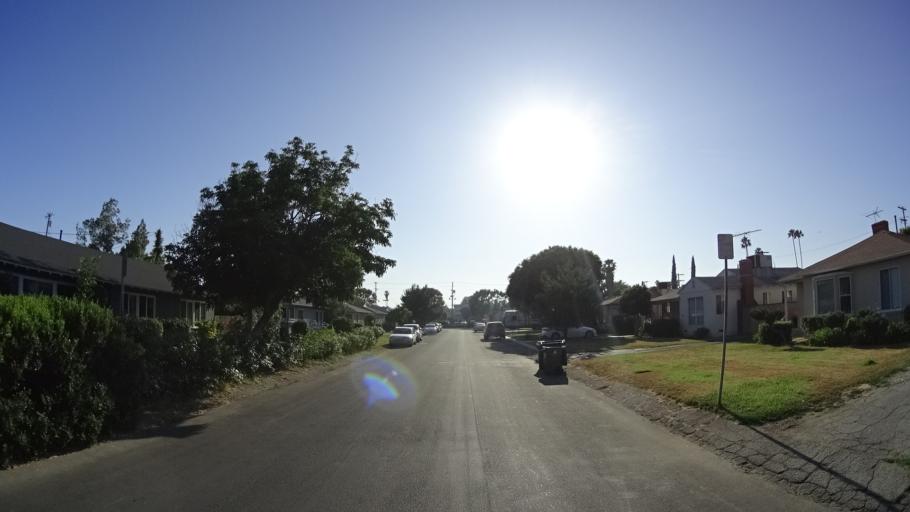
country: US
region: California
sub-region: Los Angeles County
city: Van Nuys
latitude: 34.1731
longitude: -118.4461
